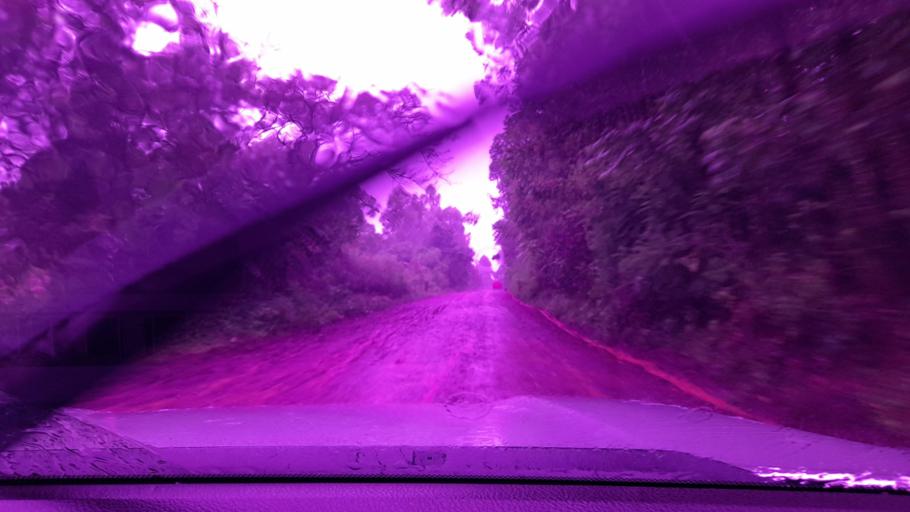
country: ET
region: Oromiya
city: Metu
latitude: 8.3442
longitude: 35.6002
